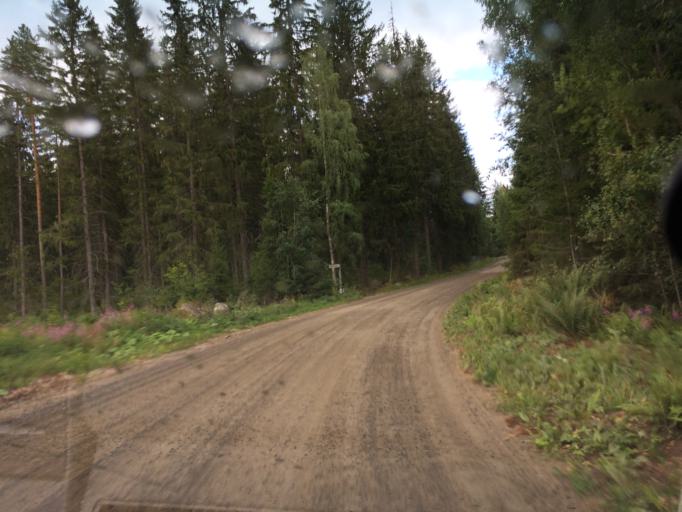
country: FI
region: Pirkanmaa
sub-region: Tampere
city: Luopioinen
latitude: 61.2710
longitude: 24.6765
